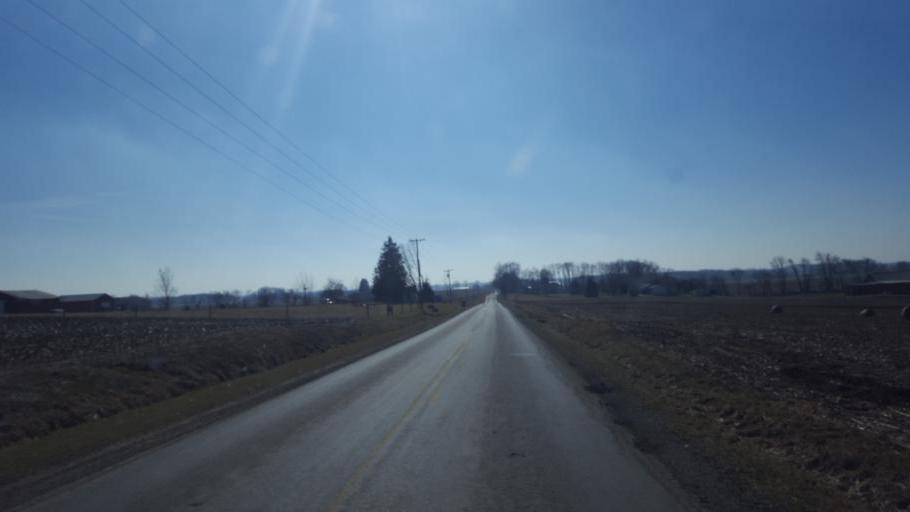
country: US
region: Ohio
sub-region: Huron County
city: Plymouth
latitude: 40.9449
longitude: -82.5832
